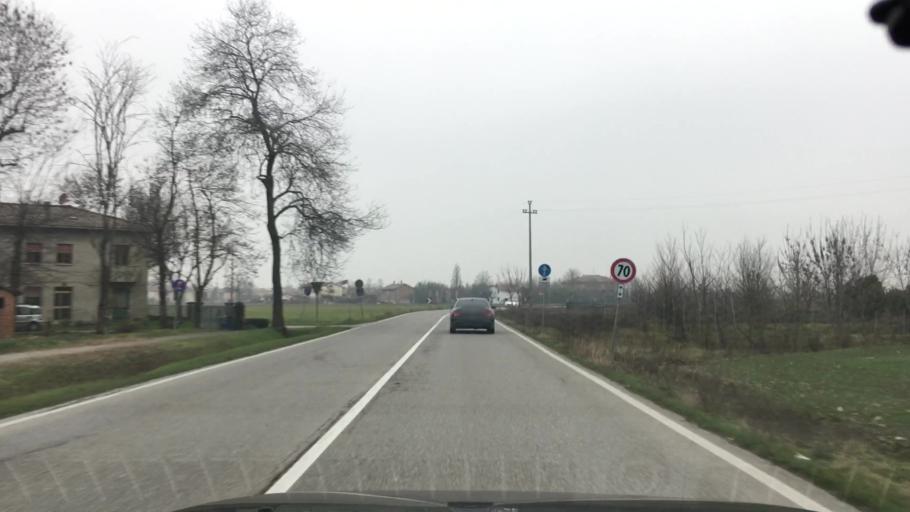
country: IT
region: Emilia-Romagna
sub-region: Provincia di Bologna
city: San Giovanni in Persiceto
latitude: 44.6337
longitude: 11.2012
